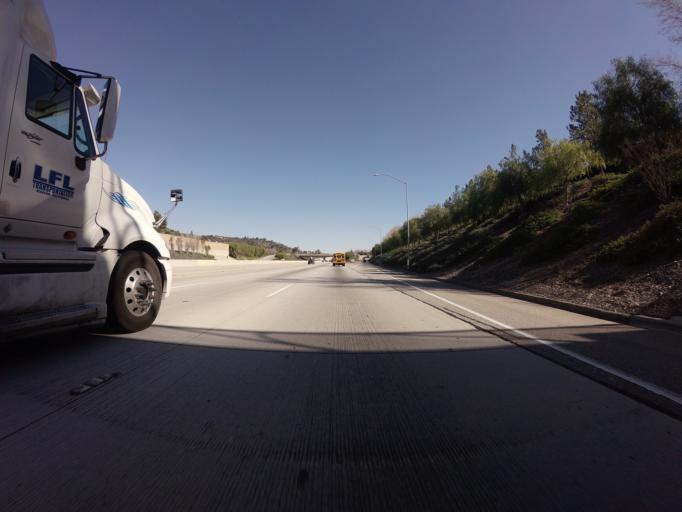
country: US
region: California
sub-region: Los Angeles County
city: Claremont
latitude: 34.1199
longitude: -117.7045
